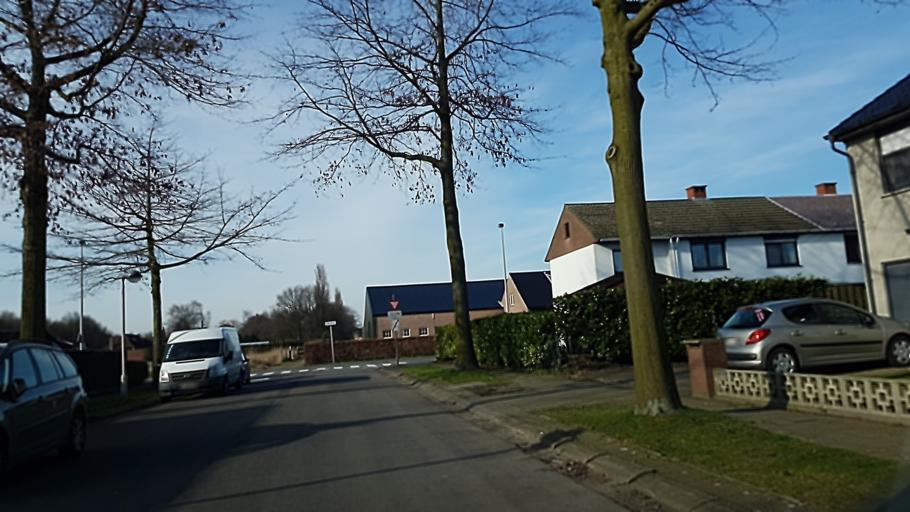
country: BE
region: Flanders
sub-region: Provincie Antwerpen
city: Stabroek
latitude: 51.3485
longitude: 4.3351
